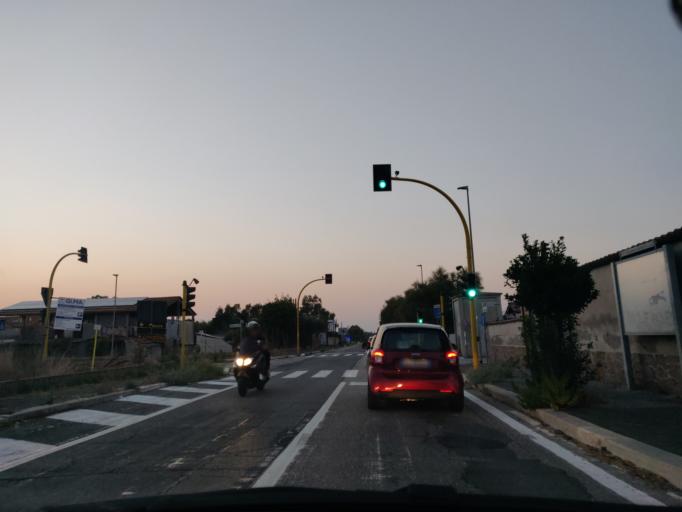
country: IT
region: Latium
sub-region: Citta metropolitana di Roma Capitale
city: Npp 23 (Parco Leonardo)
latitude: 41.8196
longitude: 12.2953
